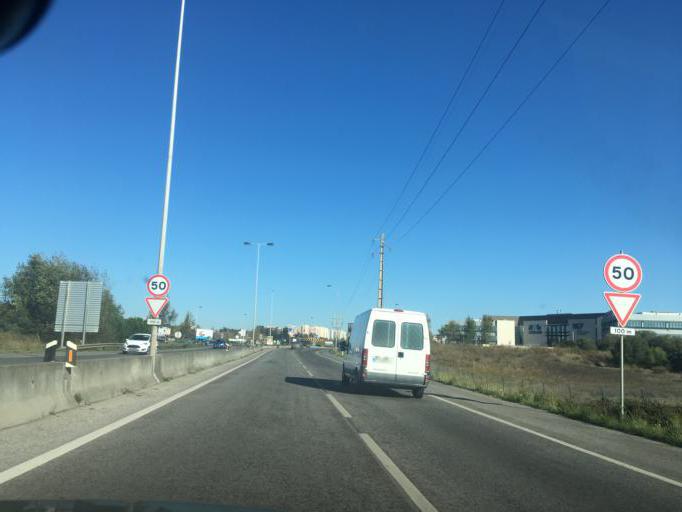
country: PT
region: Lisbon
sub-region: Oeiras
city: Porto Salvo
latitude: 38.7343
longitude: -9.2982
